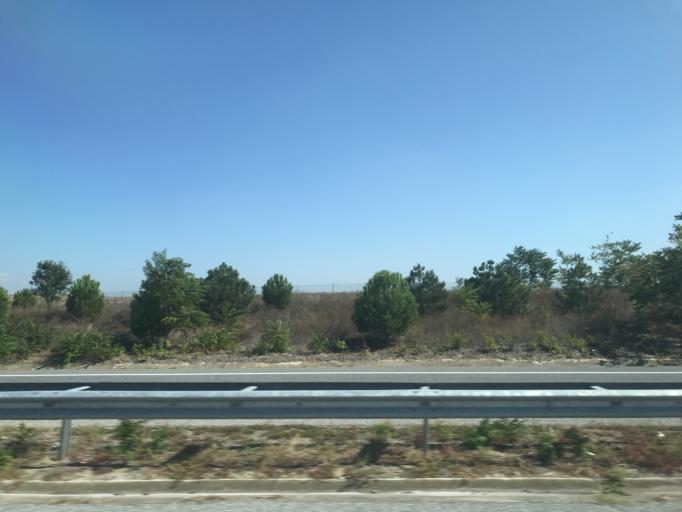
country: TR
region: Kirklareli
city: Luleburgaz
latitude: 41.4276
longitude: 27.3841
